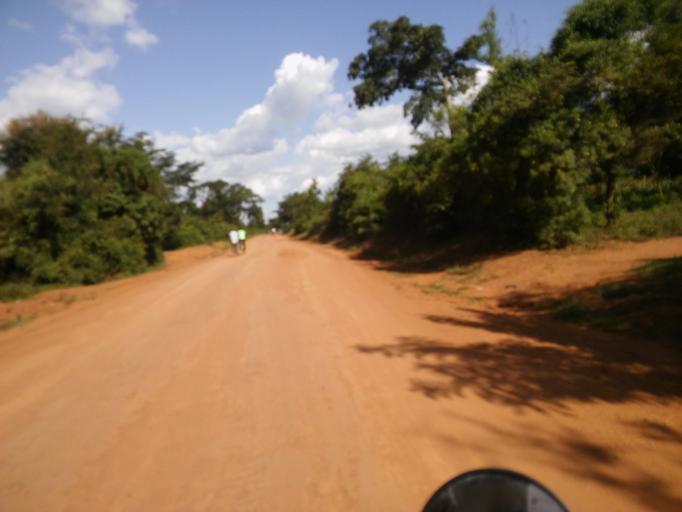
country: UG
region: Eastern Region
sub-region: Kibuku District
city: Kibuku
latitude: 1.0879
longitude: 33.7494
